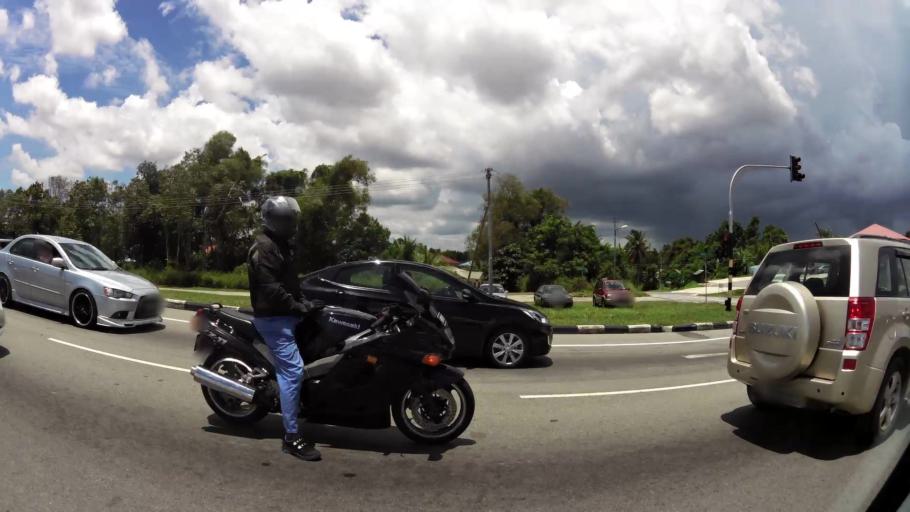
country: BN
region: Brunei and Muara
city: Bandar Seri Begawan
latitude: 4.9418
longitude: 114.9076
